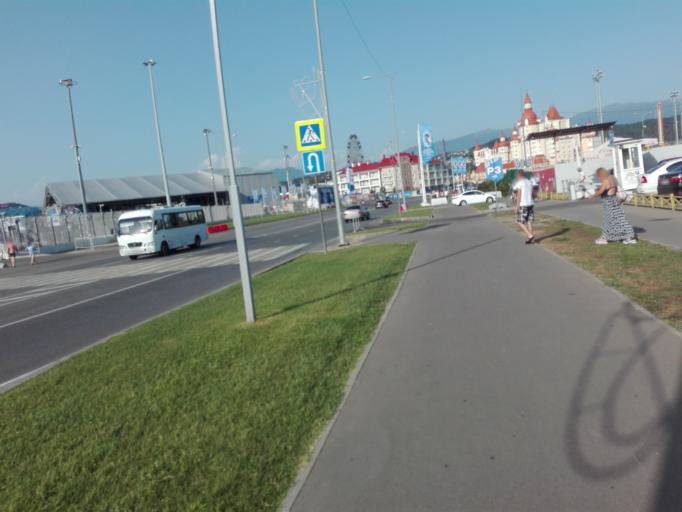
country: RU
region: Krasnodarskiy
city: Adler
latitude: 43.4009
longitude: 39.9589
